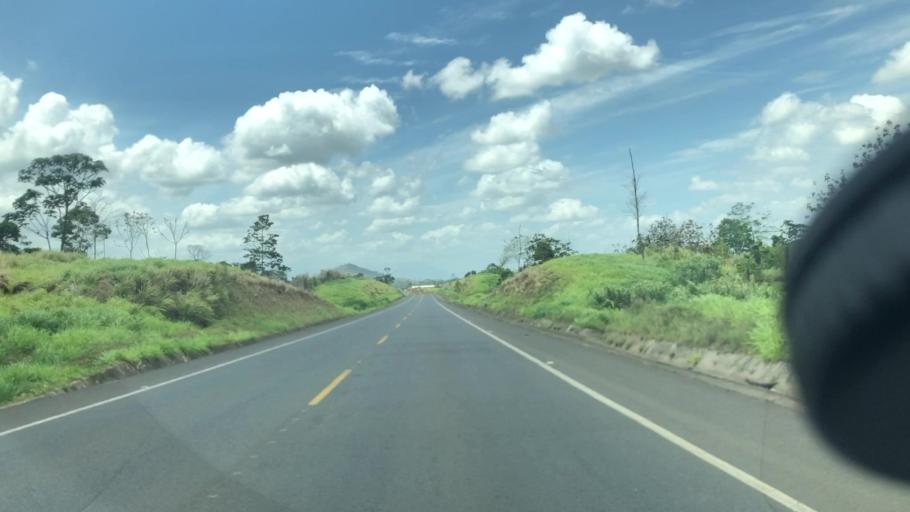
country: CR
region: Alajuela
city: Pital
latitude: 10.4345
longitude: -84.2846
